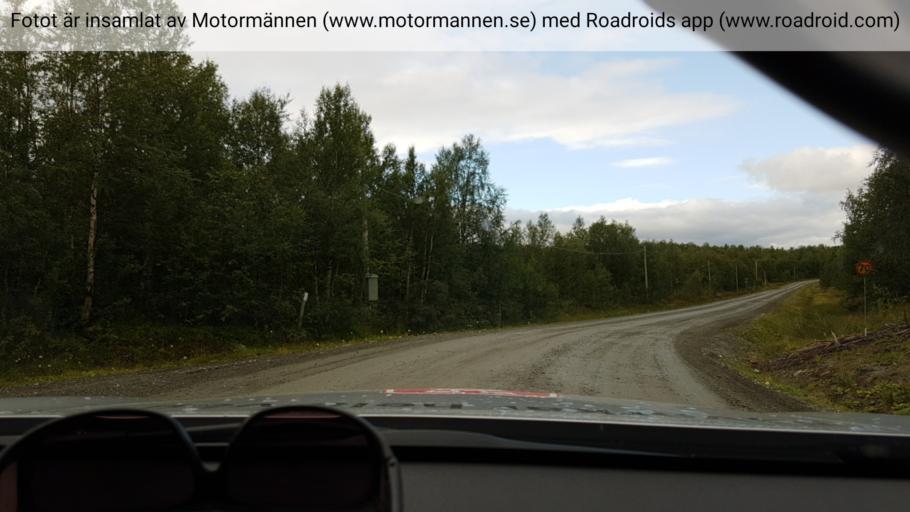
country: NO
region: Nordland
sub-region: Rana
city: Mo i Rana
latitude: 65.8348
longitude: 15.0534
